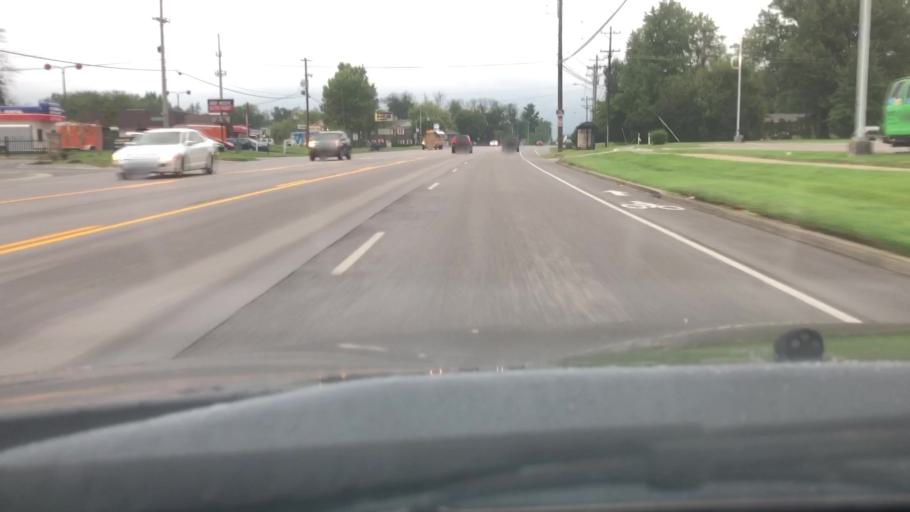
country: US
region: Kentucky
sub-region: Jefferson County
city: Hurstbourne Acres
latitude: 38.2062
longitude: -85.5811
